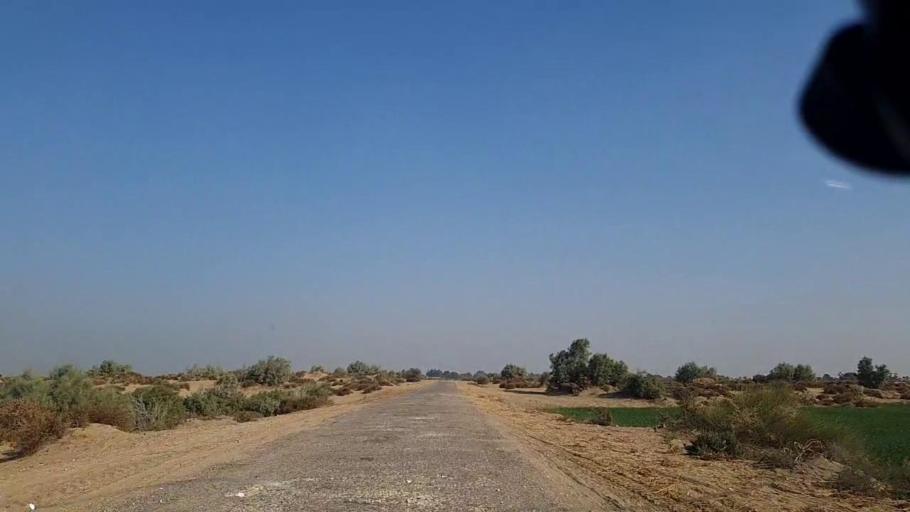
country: PK
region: Sindh
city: Khanpur
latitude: 27.6867
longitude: 69.4736
